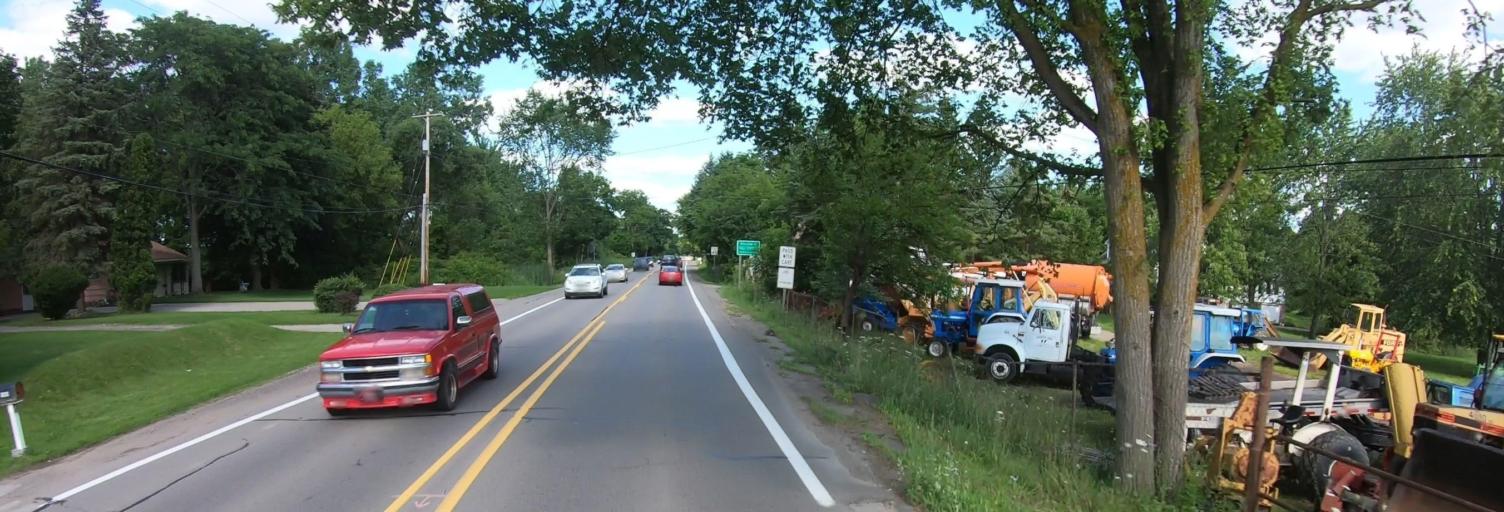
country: US
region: Michigan
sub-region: Genesee County
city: Fenton
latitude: 42.7975
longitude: -83.6861
